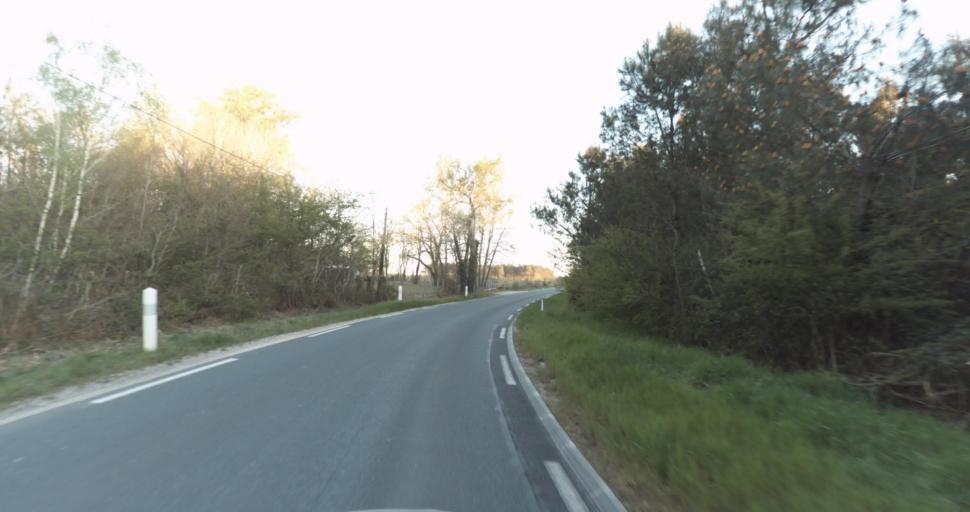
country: FR
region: Aquitaine
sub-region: Departement de la Gironde
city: Martignas-sur-Jalle
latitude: 44.8182
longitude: -0.7530
